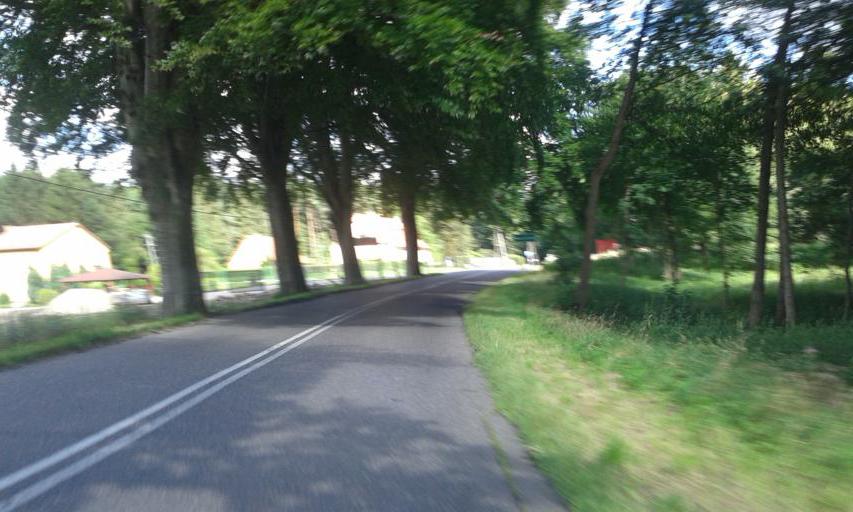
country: PL
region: West Pomeranian Voivodeship
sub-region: Powiat slawienski
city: Slawno
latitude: 54.2501
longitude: 16.6877
